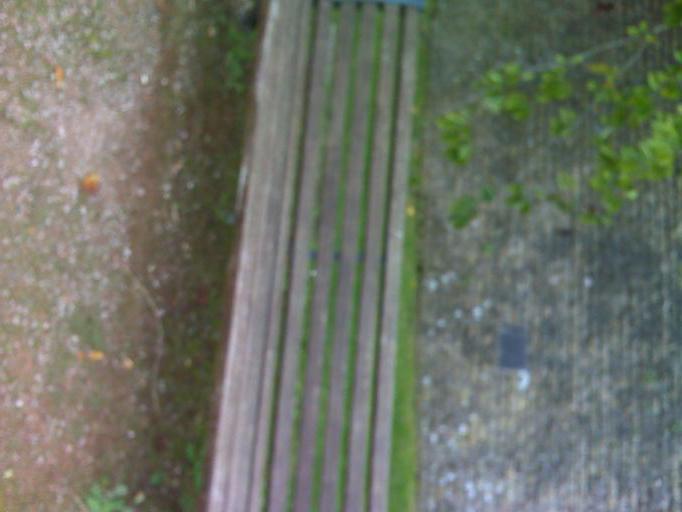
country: FR
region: Nord-Pas-de-Calais
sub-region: Departement du Nord
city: Gravelines
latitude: 50.9851
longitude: 2.1231
